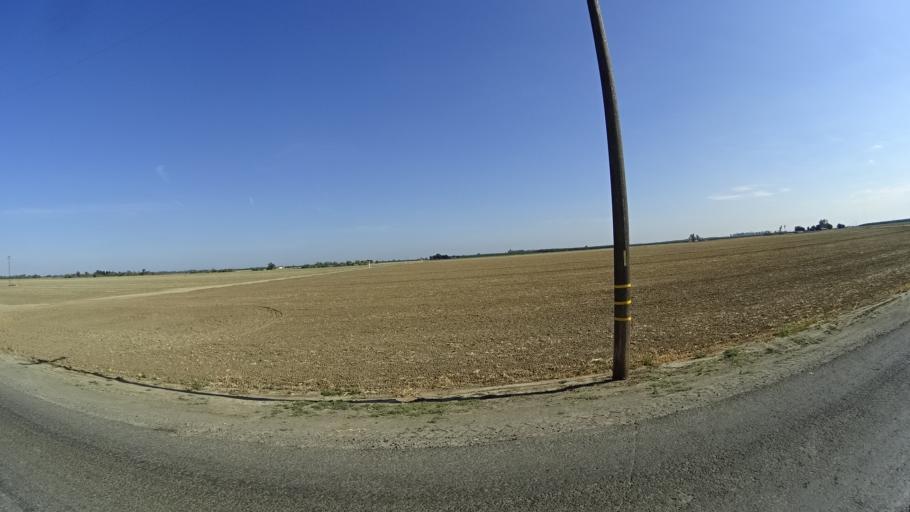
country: US
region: California
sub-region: Kings County
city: Armona
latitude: 36.2255
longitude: -119.7172
